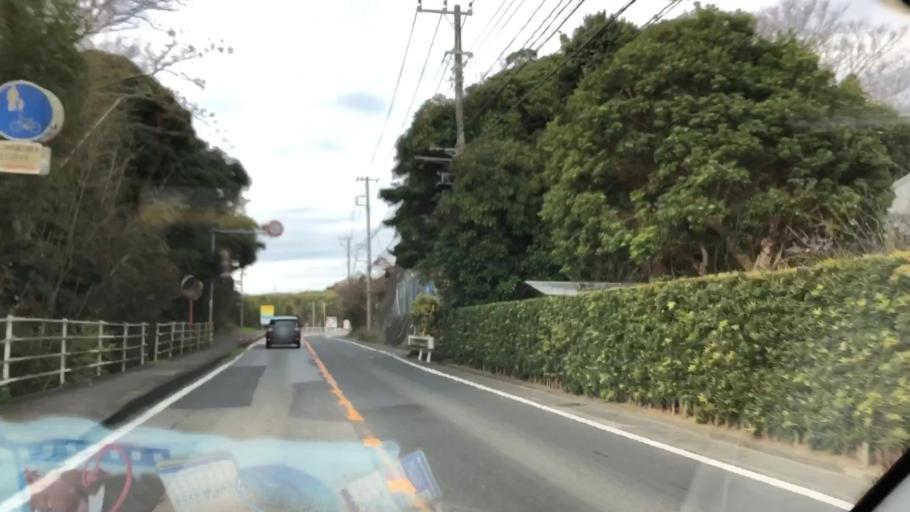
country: JP
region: Chiba
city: Tateyama
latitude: 34.9988
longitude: 139.8966
